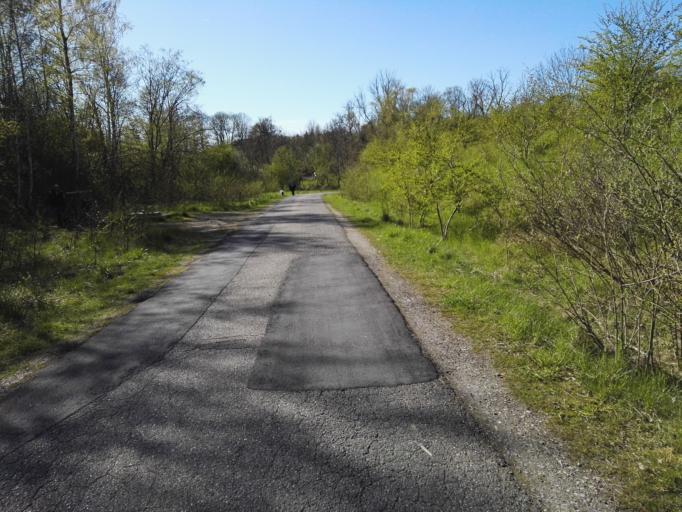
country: DK
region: Capital Region
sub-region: Egedal Kommune
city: Vekso
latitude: 55.7531
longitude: 12.2288
